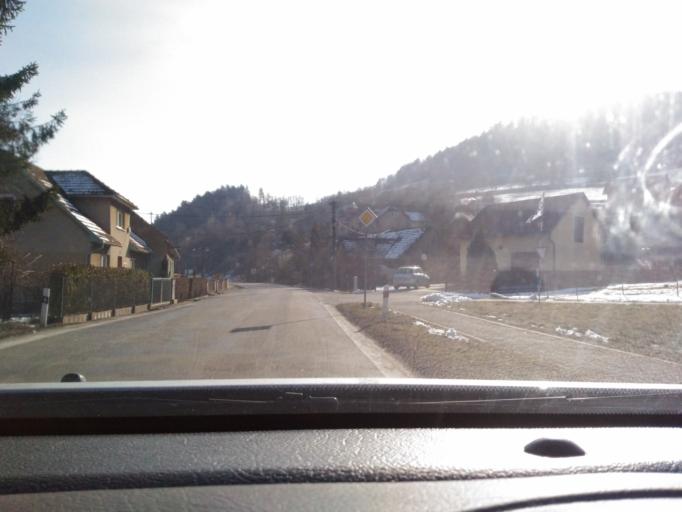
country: CZ
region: South Moravian
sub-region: Okres Brno-Venkov
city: Nedvedice
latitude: 49.4871
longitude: 16.3330
